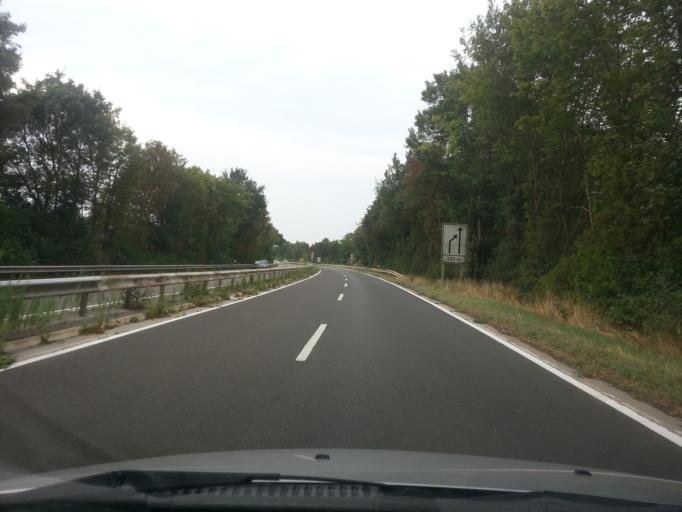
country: DE
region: Rheinland-Pfalz
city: Worms
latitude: 49.6178
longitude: 8.3604
